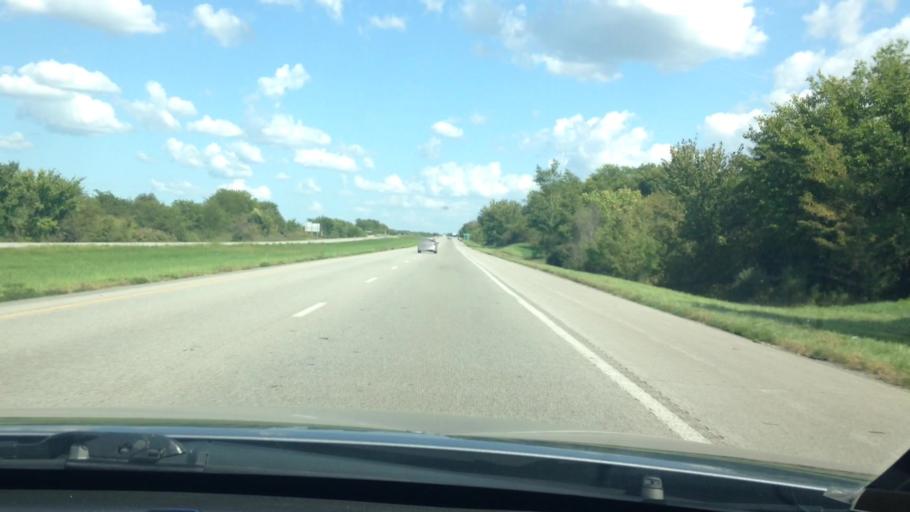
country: US
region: Missouri
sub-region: Clay County
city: Smithville
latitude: 39.3109
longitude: -94.5398
